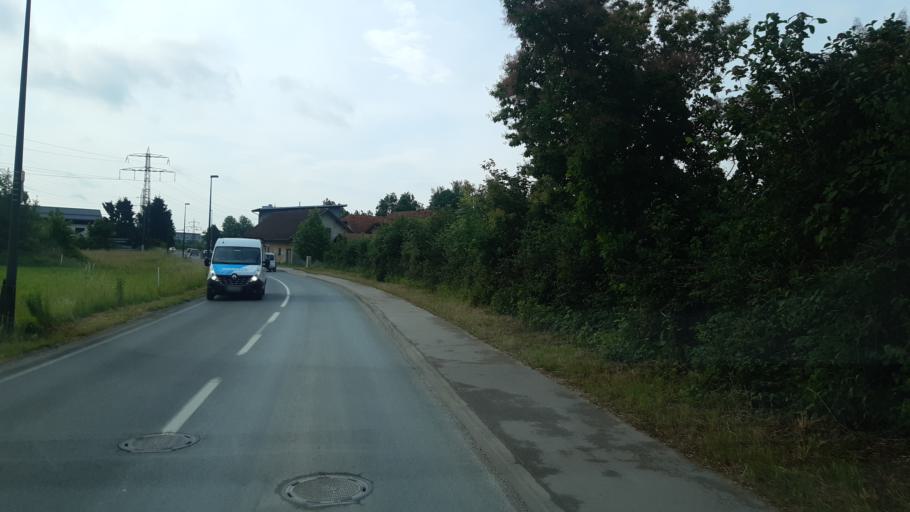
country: SI
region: Medvode
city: Zgornje Pirnice
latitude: 46.1198
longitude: 14.4499
